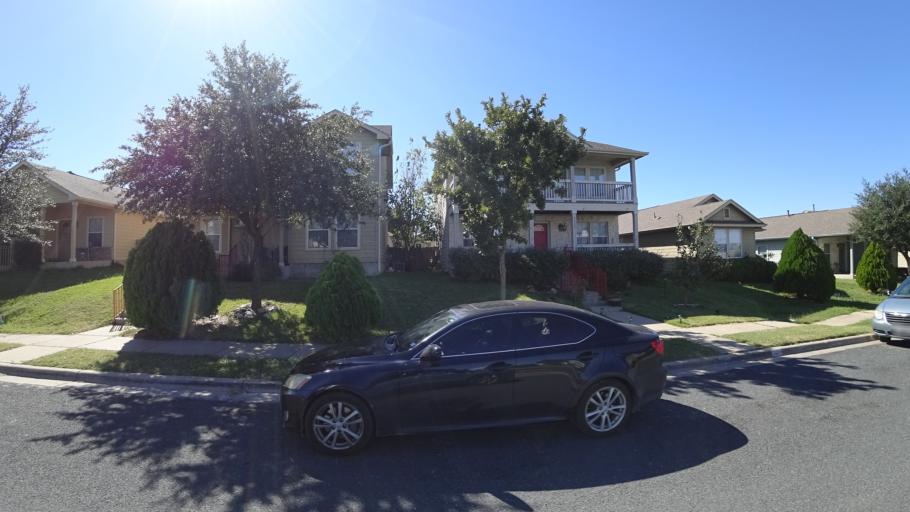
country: US
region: Texas
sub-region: Travis County
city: Hornsby Bend
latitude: 30.2909
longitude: -97.6441
